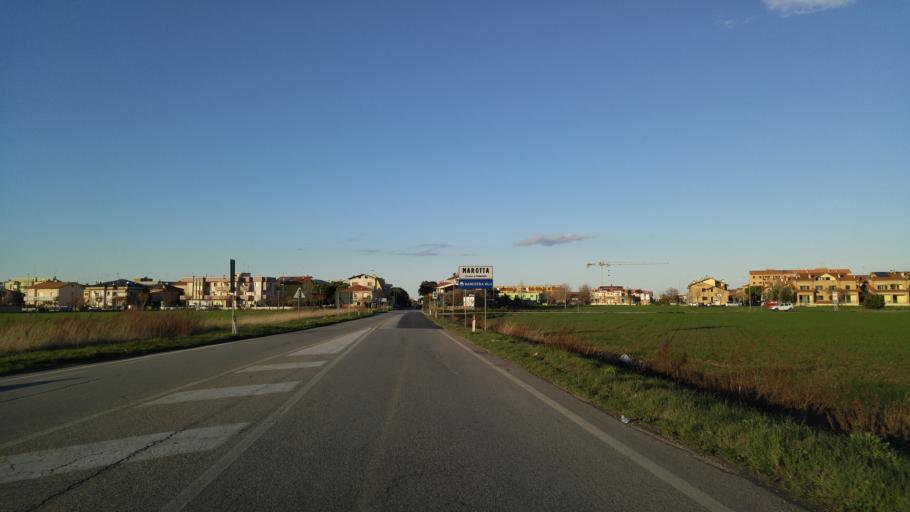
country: IT
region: The Marches
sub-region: Provincia di Pesaro e Urbino
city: Marotta
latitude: 43.7618
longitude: 13.1370
